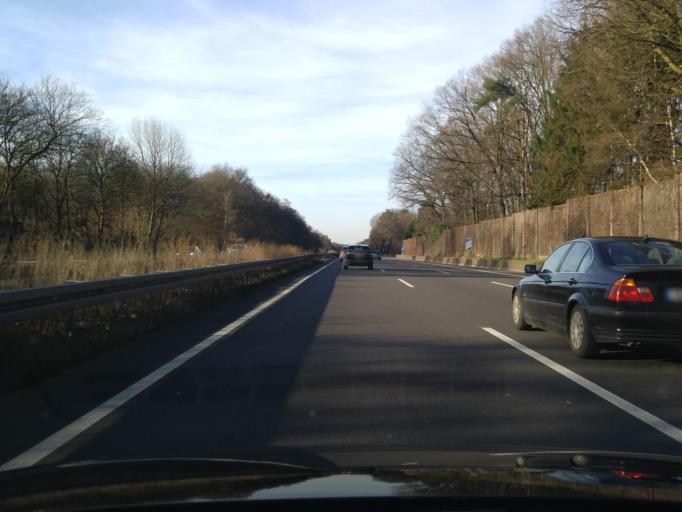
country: DE
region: North Rhine-Westphalia
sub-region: Regierungsbezirk Koln
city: Rosrath
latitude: 50.8959
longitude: 7.1628
